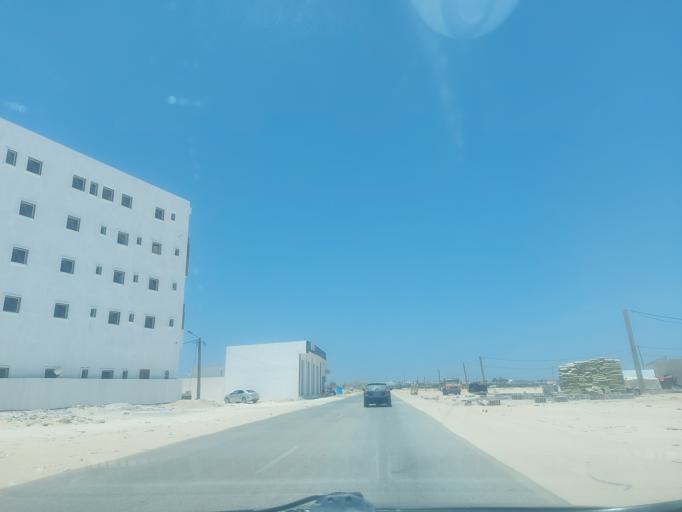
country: MR
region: Nouakchott
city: Nouakchott
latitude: 18.0865
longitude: -15.9529
